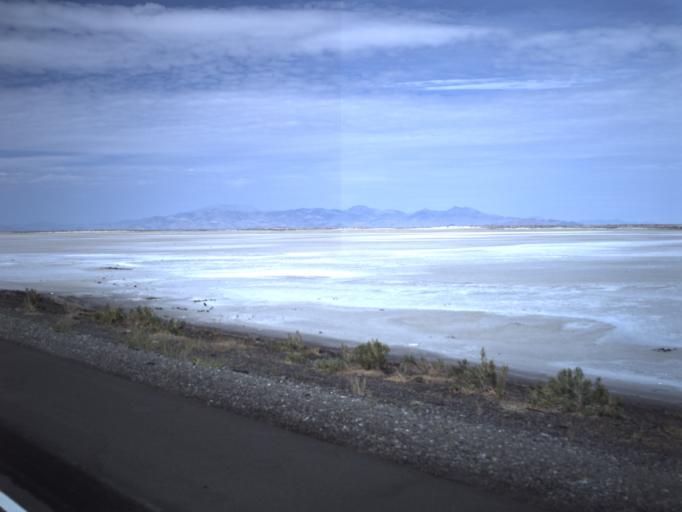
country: US
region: Utah
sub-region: Tooele County
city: Wendover
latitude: 40.7304
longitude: -113.4394
